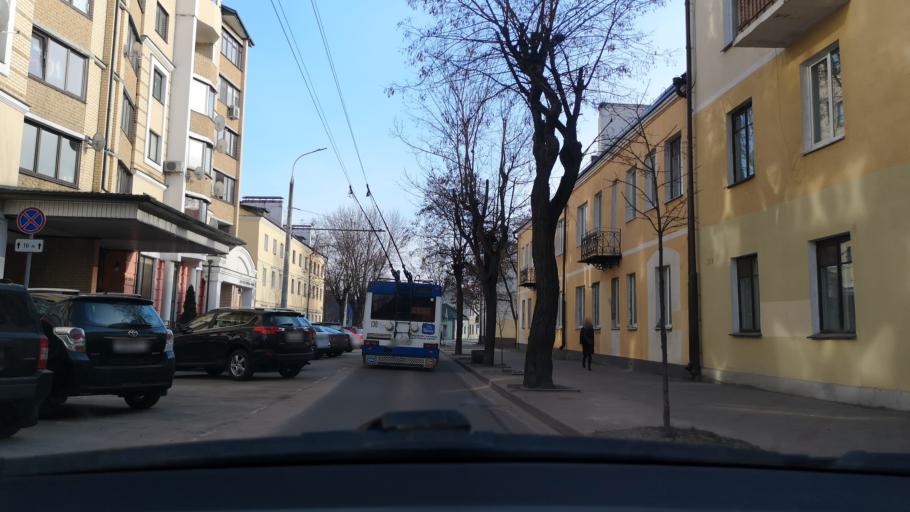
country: BY
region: Brest
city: Brest
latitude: 52.0933
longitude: 23.6903
